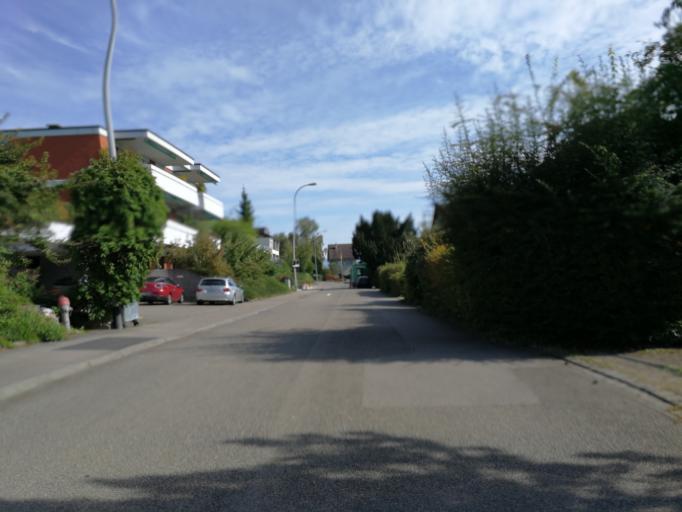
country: CH
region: Zurich
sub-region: Bezirk Meilen
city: Mannedorf
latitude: 47.2518
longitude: 8.7015
